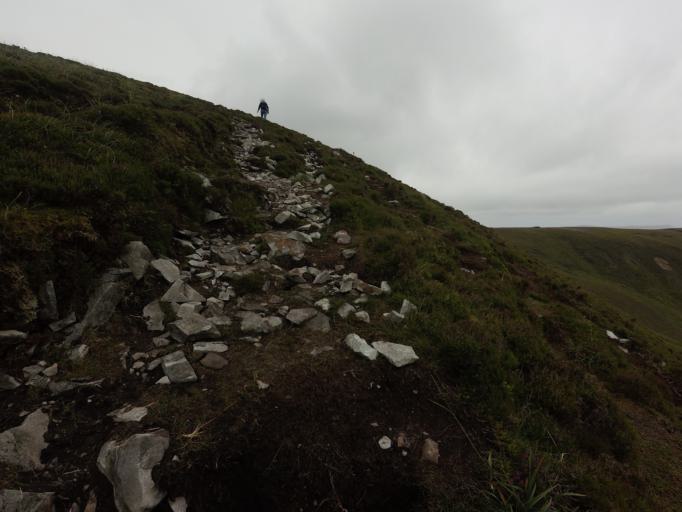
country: IE
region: Ulster
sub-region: County Donegal
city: Killybegs
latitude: 54.6454
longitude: -8.6881
